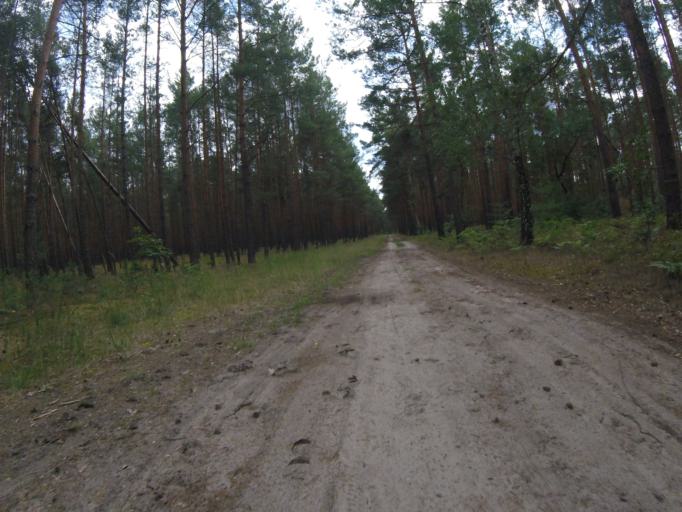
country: DE
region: Brandenburg
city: Halbe
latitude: 52.1363
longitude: 13.6958
